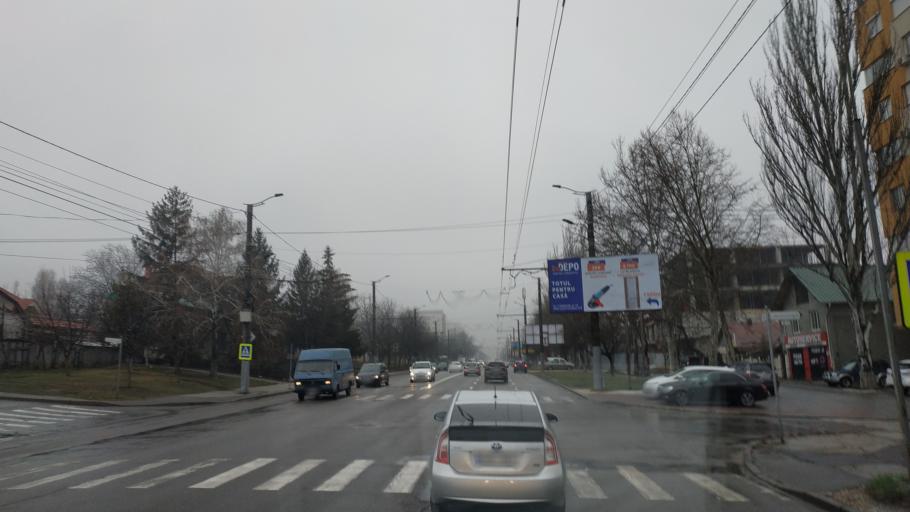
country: MD
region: Chisinau
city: Vatra
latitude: 47.0307
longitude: 28.7856
